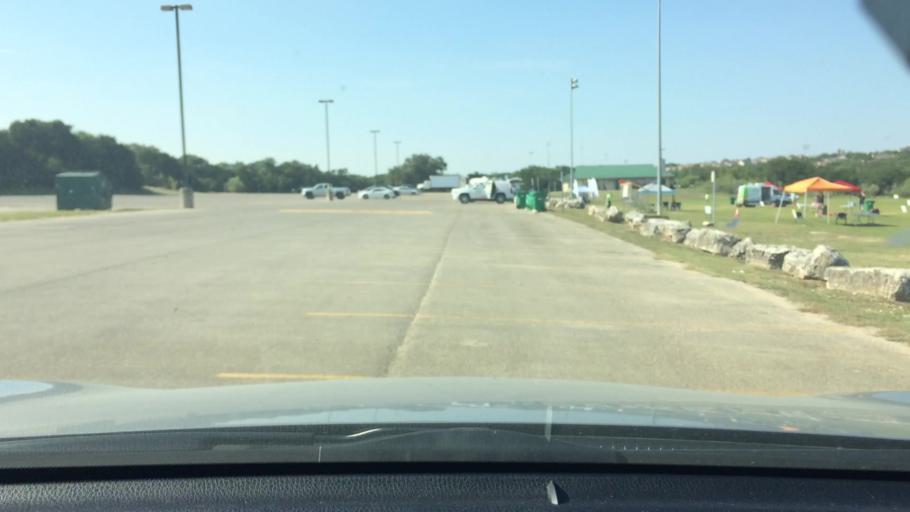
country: US
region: Texas
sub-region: Bexar County
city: Hollywood Park
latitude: 29.6452
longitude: -98.5166
